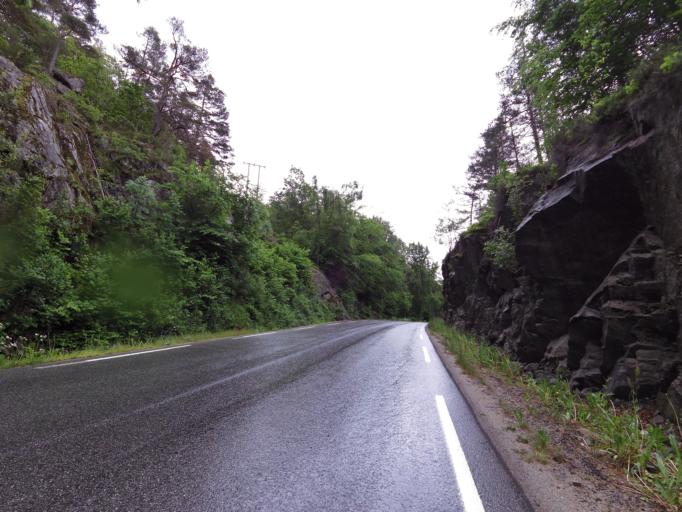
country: NO
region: Vest-Agder
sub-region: Mandal
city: Mandal
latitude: 58.0241
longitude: 7.5171
